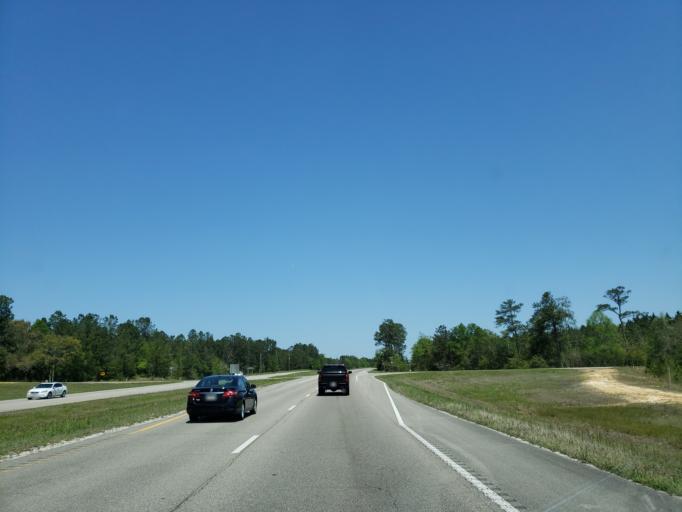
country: US
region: Mississippi
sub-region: Harrison County
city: Saucier
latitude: 30.6441
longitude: -89.1331
